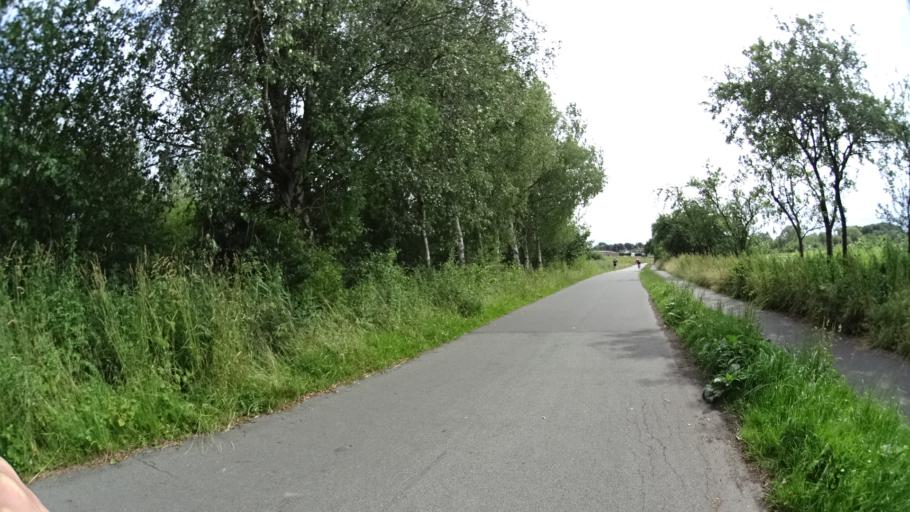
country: DK
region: Central Jutland
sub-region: Arhus Kommune
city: Arhus
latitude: 56.1424
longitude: 10.1735
